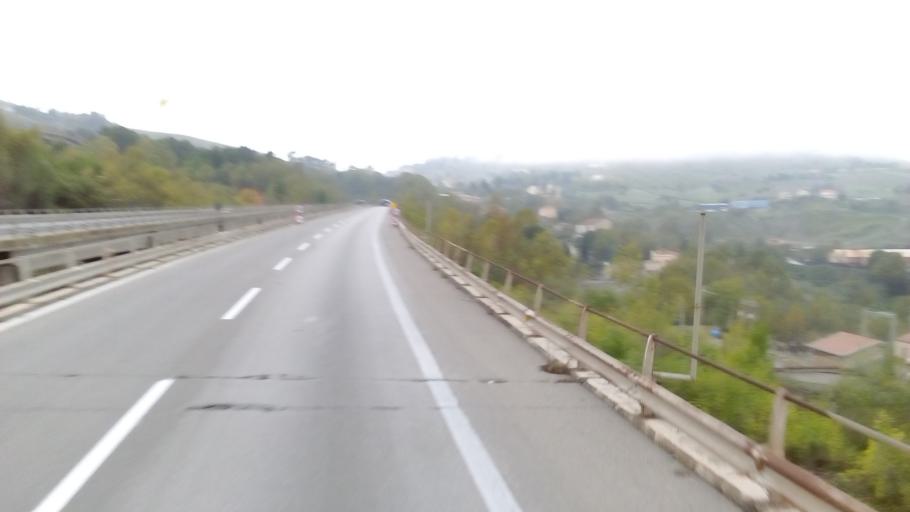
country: IT
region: Sicily
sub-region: Enna
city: Enna
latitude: 37.5787
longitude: 14.2945
